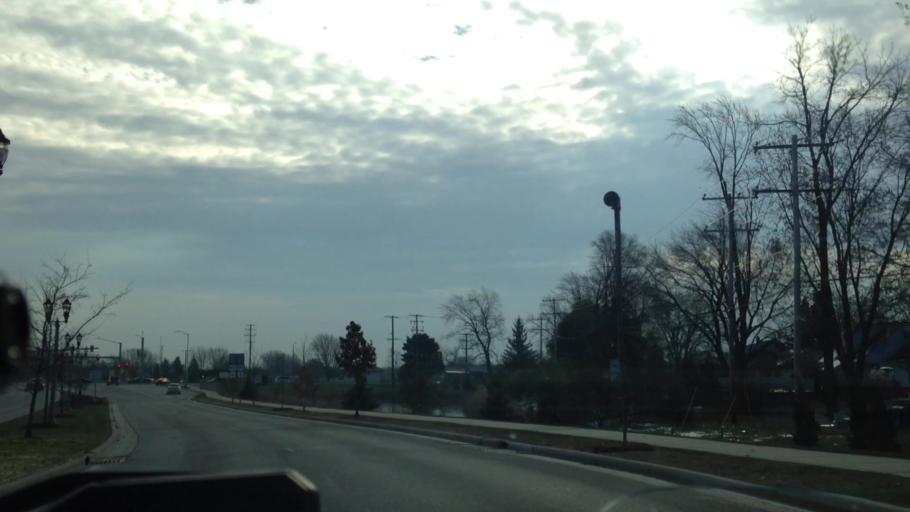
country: US
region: Wisconsin
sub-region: Waukesha County
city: Menomonee Falls
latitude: 43.1819
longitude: -88.1056
